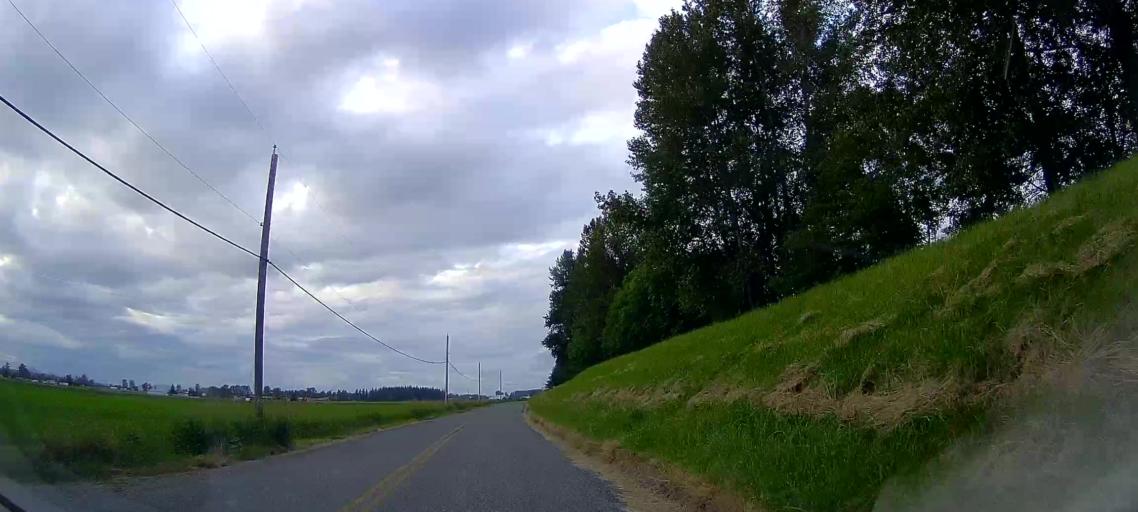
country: US
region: Washington
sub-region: Skagit County
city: Mount Vernon
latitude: 48.3515
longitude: -122.3624
